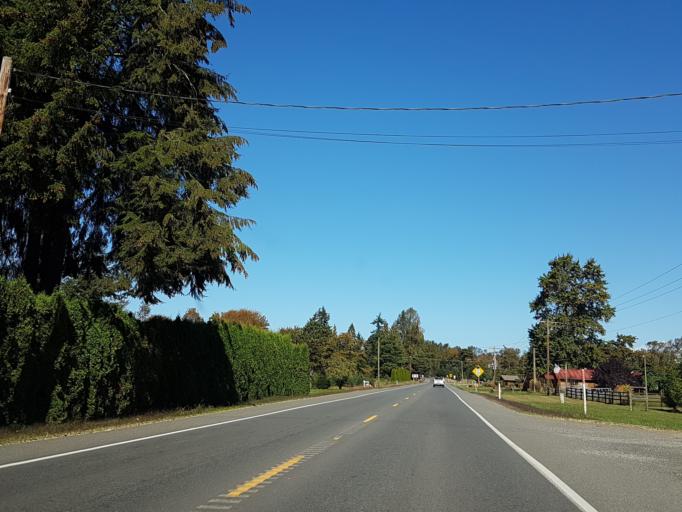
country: US
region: Washington
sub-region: Snohomish County
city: Monroe
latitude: 47.8383
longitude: -121.9693
